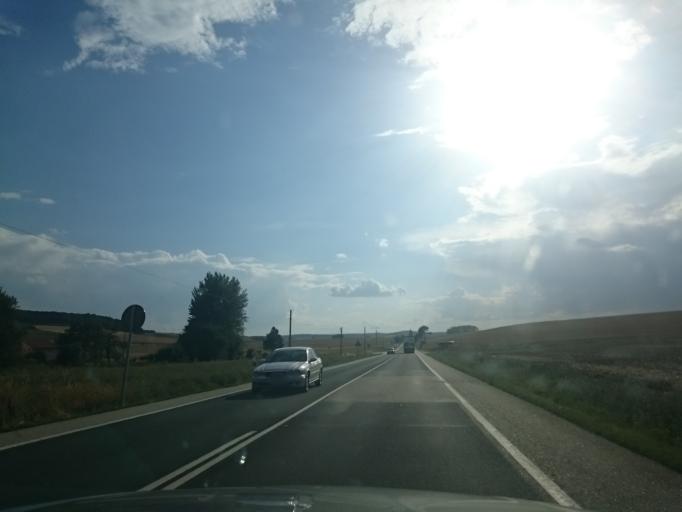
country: ES
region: Castille and Leon
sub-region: Provincia de Burgos
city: Tosantos
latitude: 42.4087
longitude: -3.2609
